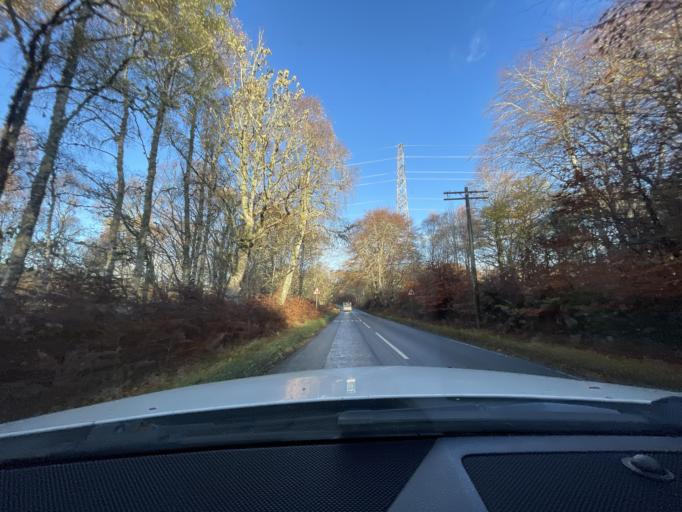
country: GB
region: Scotland
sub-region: Highland
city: Inverness
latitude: 57.4398
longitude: -4.2641
